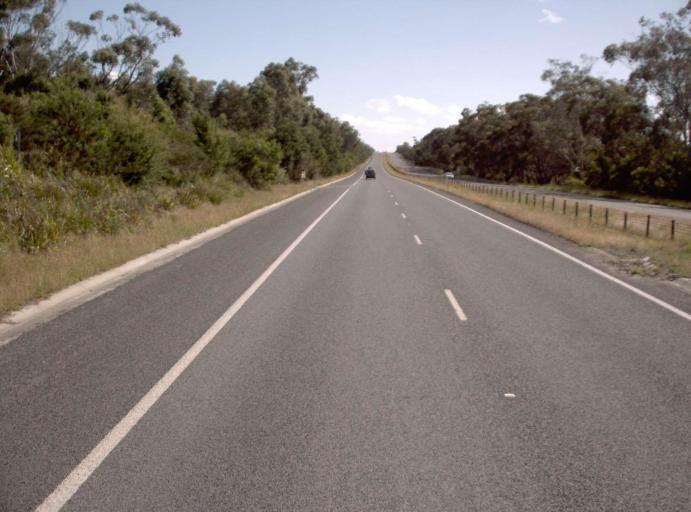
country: AU
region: Victoria
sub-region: Cardinia
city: Koo-Wee-Rup
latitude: -38.3833
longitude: 145.5515
